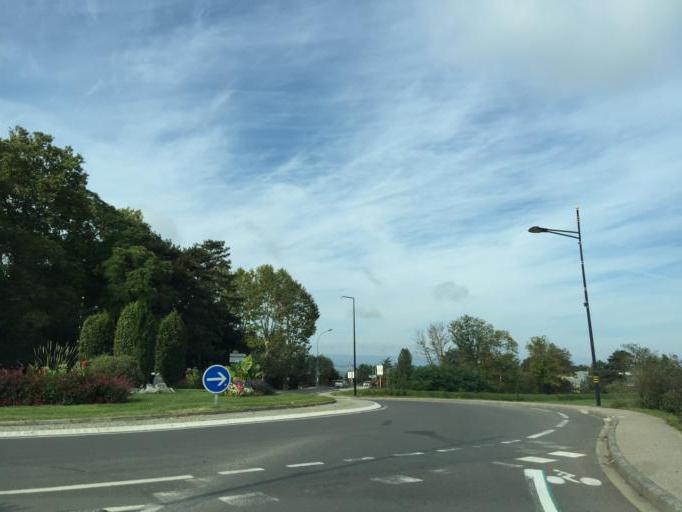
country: FR
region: Rhone-Alpes
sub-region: Departement de la Loire
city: Sury-le-Comtal
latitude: 45.5411
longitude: 4.1808
